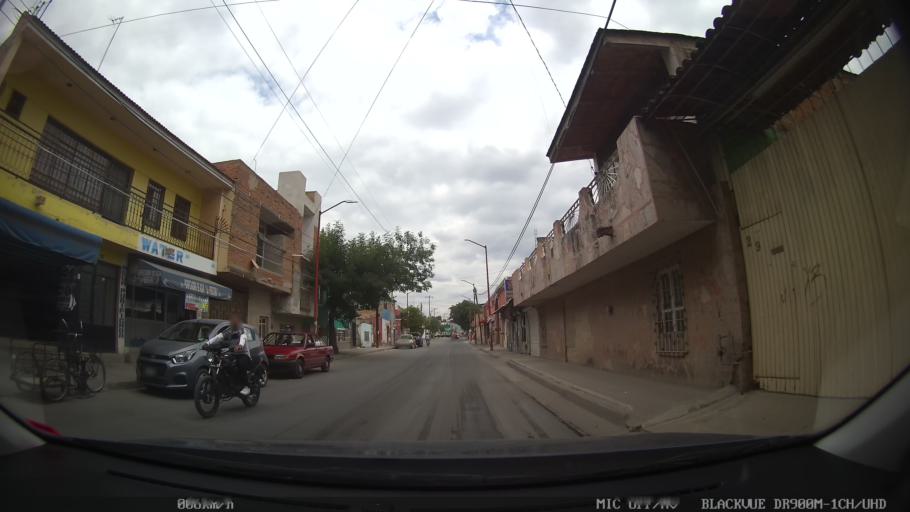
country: MX
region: Jalisco
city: Tonala
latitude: 20.6517
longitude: -103.2528
